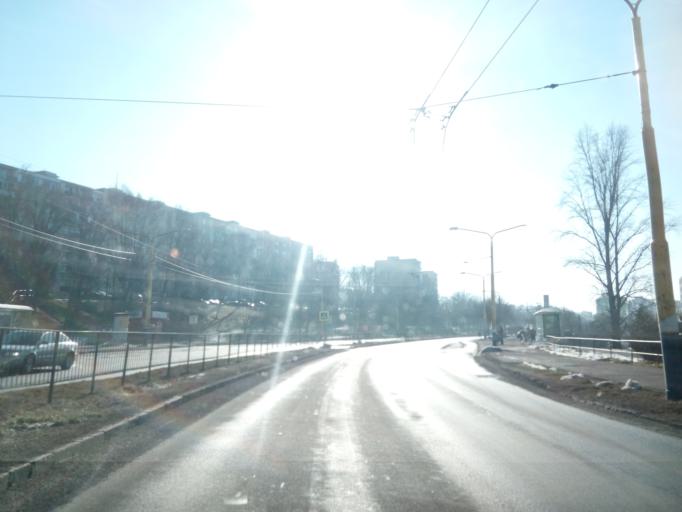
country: SK
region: Kosicky
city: Kosice
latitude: 48.7427
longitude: 21.2799
